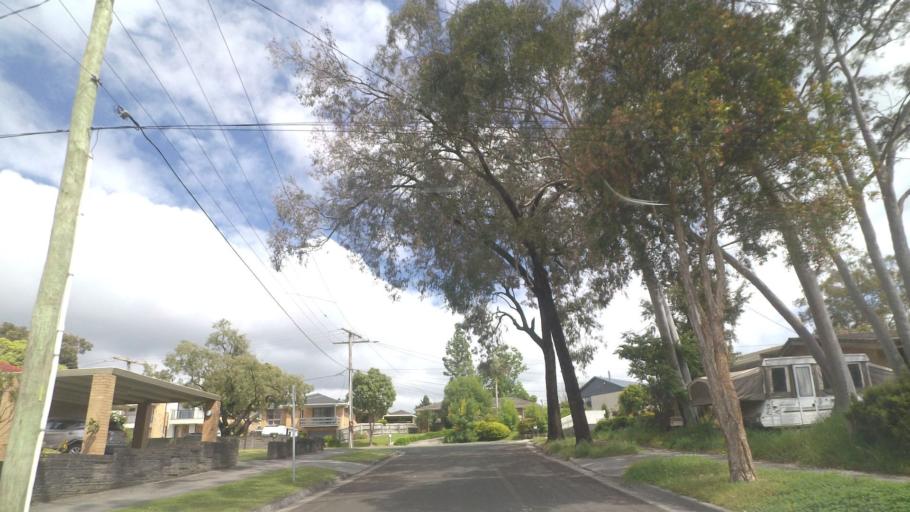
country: AU
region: Victoria
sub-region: Knox
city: Bayswater
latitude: -37.8451
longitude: 145.2661
